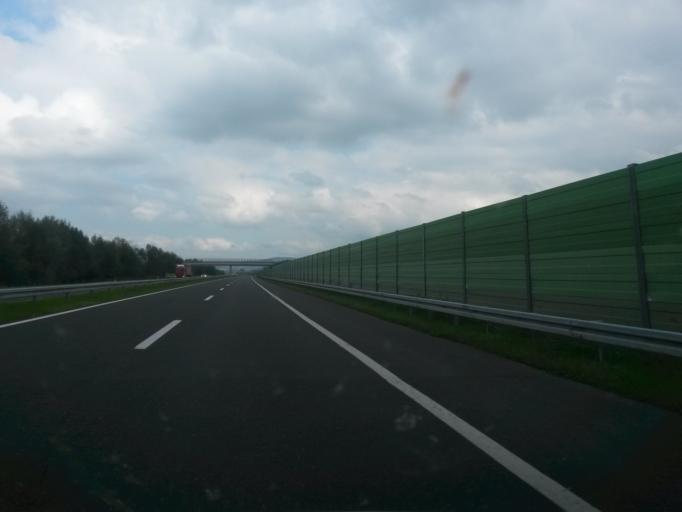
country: HR
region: Varazdinska
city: Remetinec
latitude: 46.0324
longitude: 16.2953
